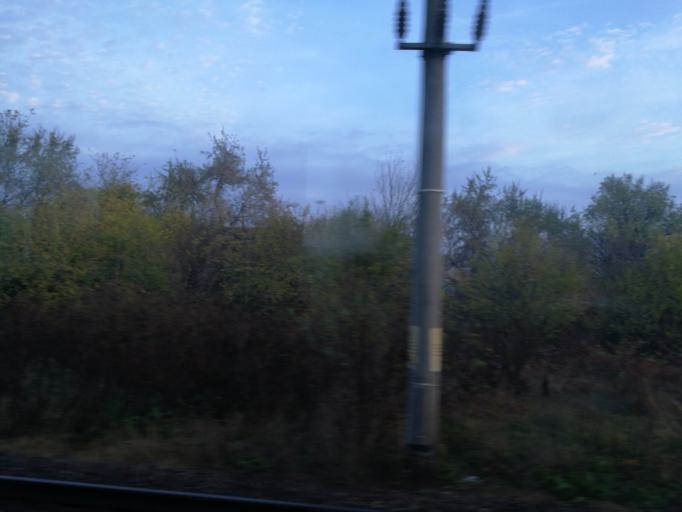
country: RO
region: Prahova
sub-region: Comuna Albesti-Paleologu
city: Albesti-Paleologu
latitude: 44.9435
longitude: 26.2399
